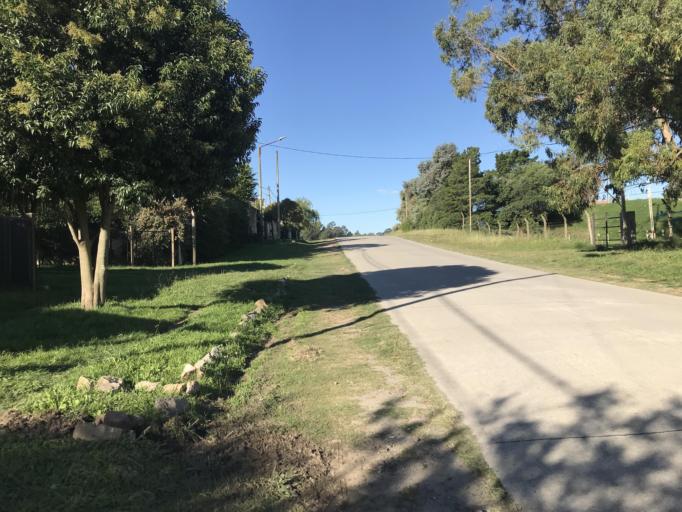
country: AR
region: Buenos Aires
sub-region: Partido de Tandil
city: Tandil
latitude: -37.3390
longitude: -59.1161
